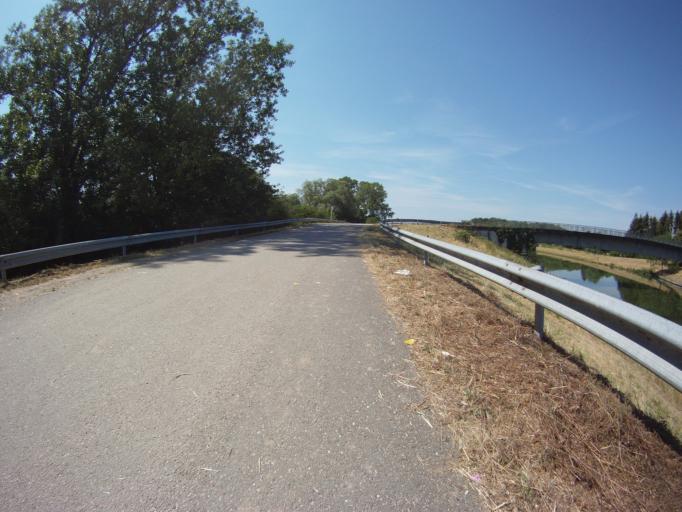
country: FR
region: Lorraine
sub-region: Departement de Meurthe-et-Moselle
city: Toul
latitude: 48.6820
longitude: 5.9061
